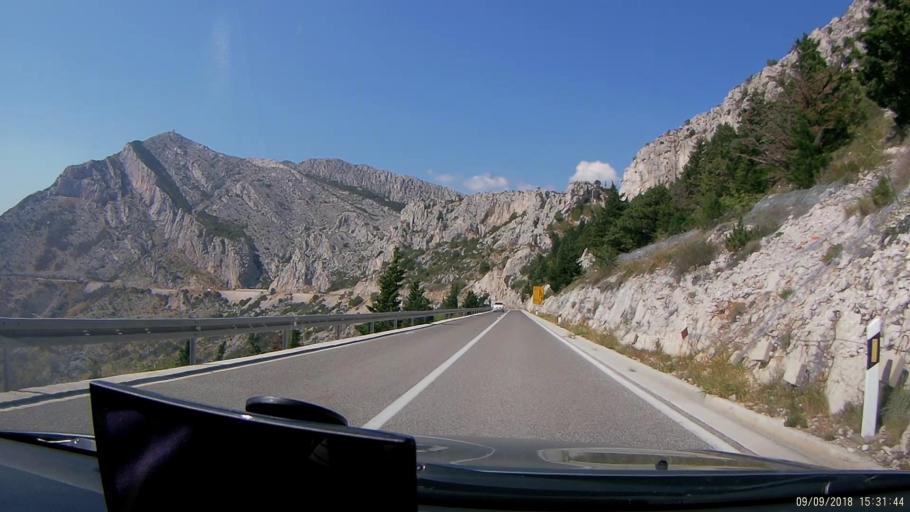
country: HR
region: Splitsko-Dalmatinska
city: Donja Brela
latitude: 43.3998
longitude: 16.8941
